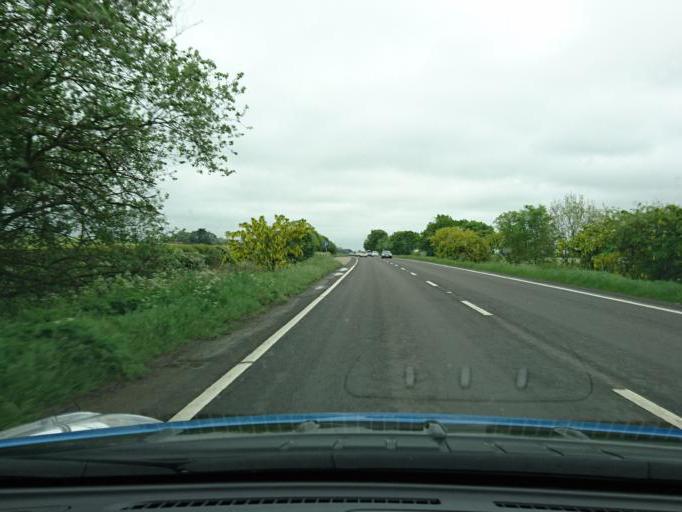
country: GB
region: England
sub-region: Oxfordshire
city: Faringdon
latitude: 51.6575
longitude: -1.5660
